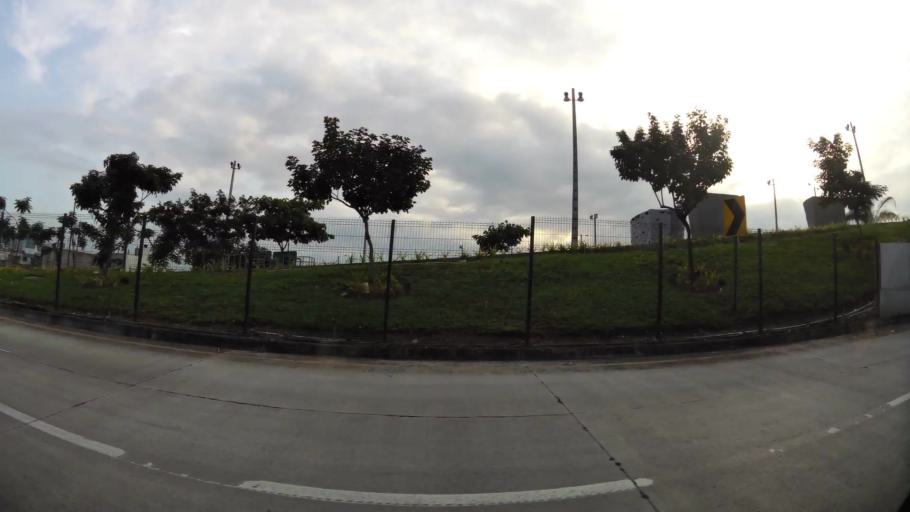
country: EC
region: Guayas
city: Eloy Alfaro
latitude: -2.1386
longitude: -79.8824
